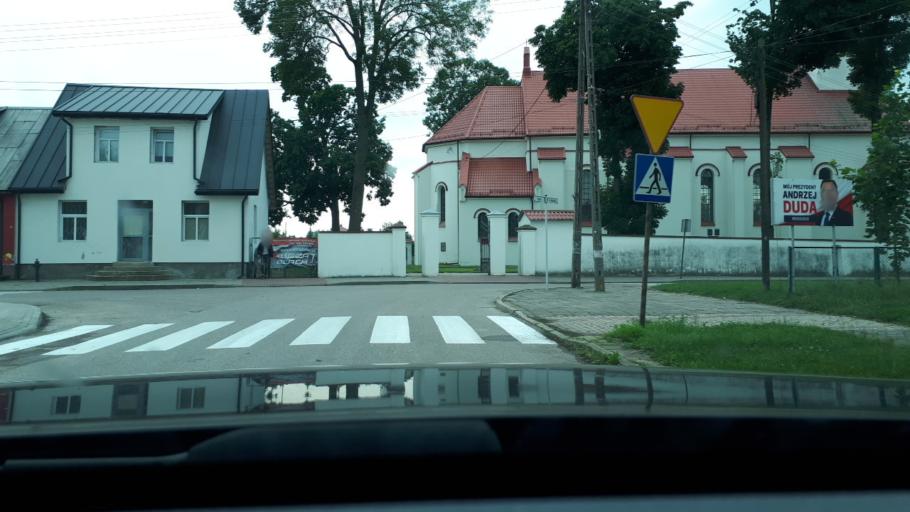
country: PL
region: Podlasie
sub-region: Powiat moniecki
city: Knyszyn
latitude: 53.3122
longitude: 22.9178
